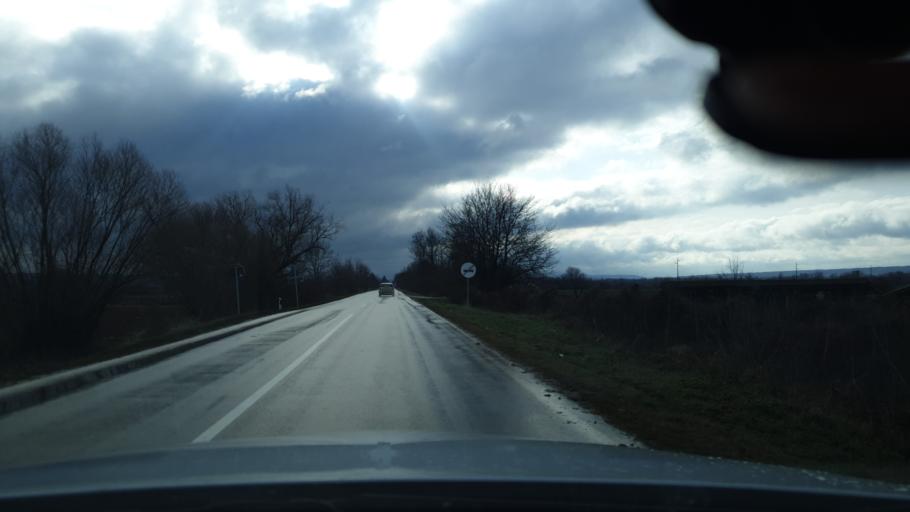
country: RS
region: Central Serbia
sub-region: Branicevski Okrug
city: Malo Crnice
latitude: 44.5081
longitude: 21.3237
